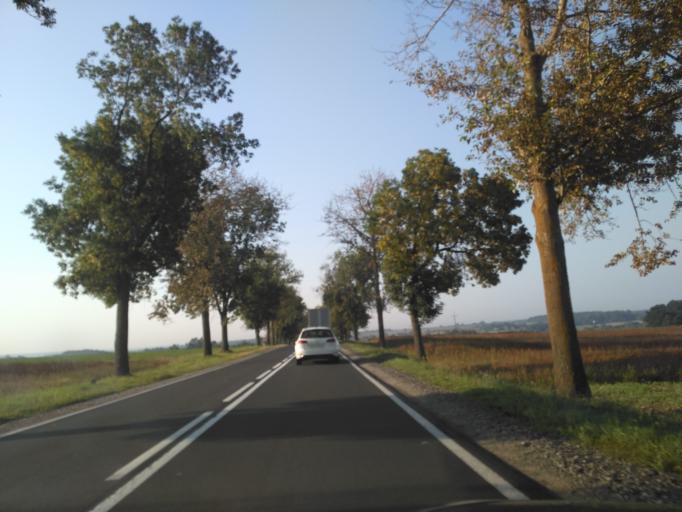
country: PL
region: Lublin Voivodeship
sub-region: Powiat krasnicki
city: Szastarka
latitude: 50.8106
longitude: 22.3195
